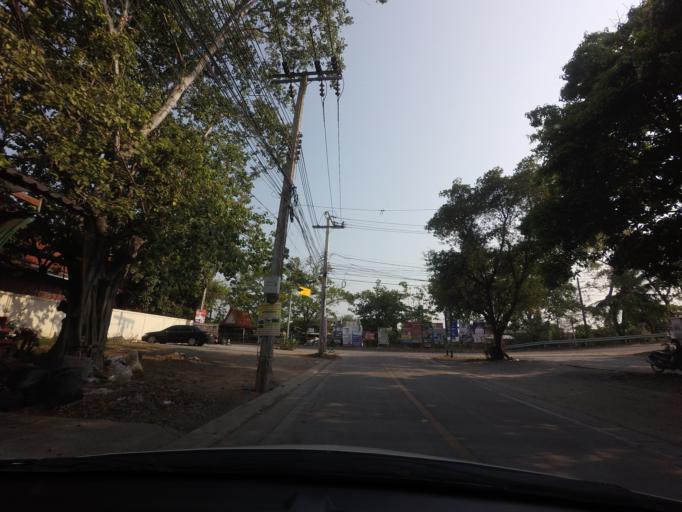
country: TH
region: Nonthaburi
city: Bang Yai
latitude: 13.8030
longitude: 100.3741
